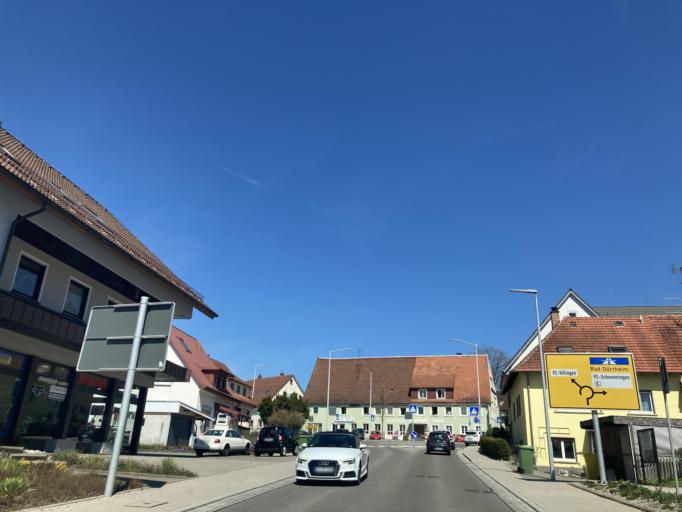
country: DE
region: Baden-Wuerttemberg
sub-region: Freiburg Region
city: Villingen-Schwenningen
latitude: 48.0313
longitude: 8.4711
